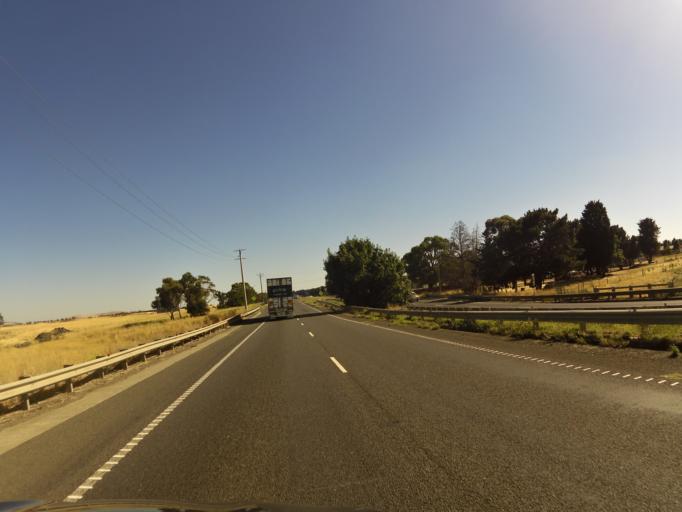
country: AU
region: Victoria
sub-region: Hume
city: Craigieburn
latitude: -37.5287
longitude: 144.9473
